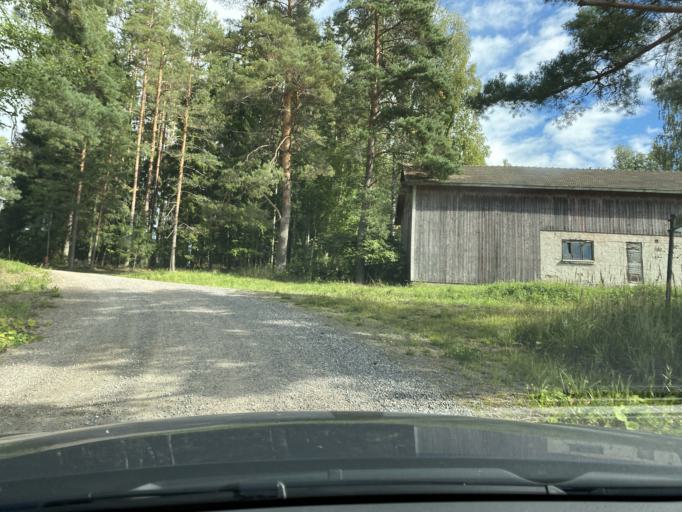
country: FI
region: Haeme
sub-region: Forssa
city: Humppila
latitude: 61.0632
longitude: 23.2709
